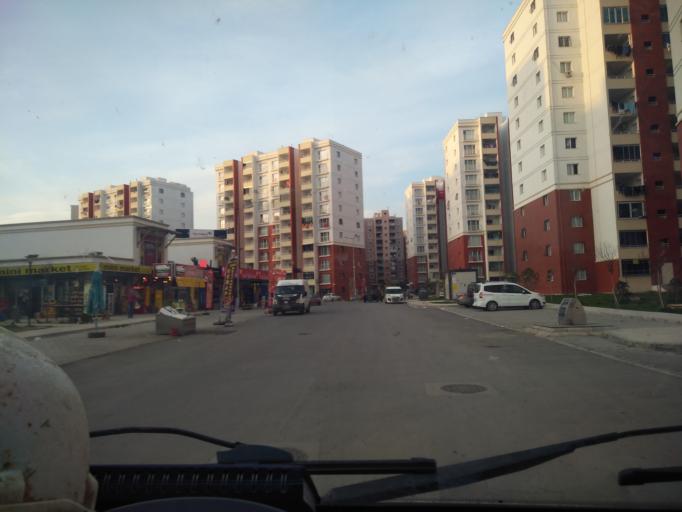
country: TR
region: Adana
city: Seyhan
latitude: 37.0081
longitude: 35.2779
